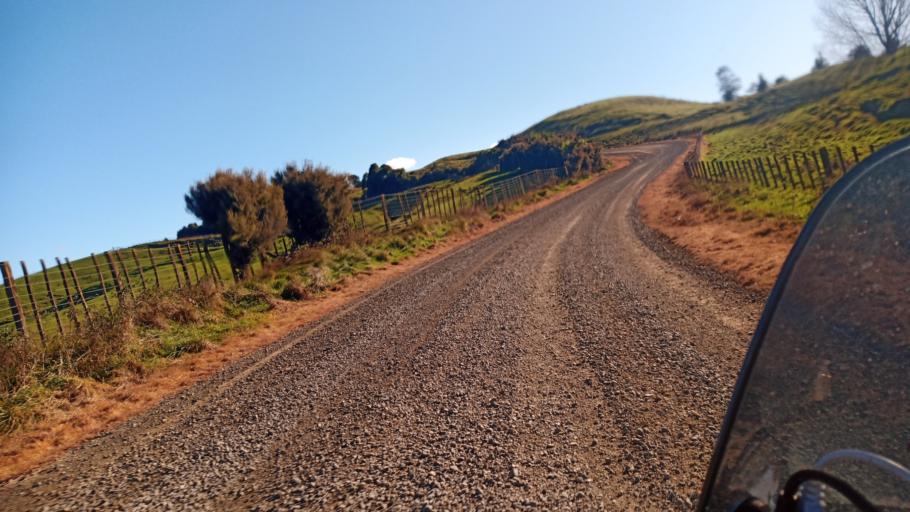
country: NZ
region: Hawke's Bay
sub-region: Wairoa District
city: Wairoa
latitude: -38.8011
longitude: 177.2883
